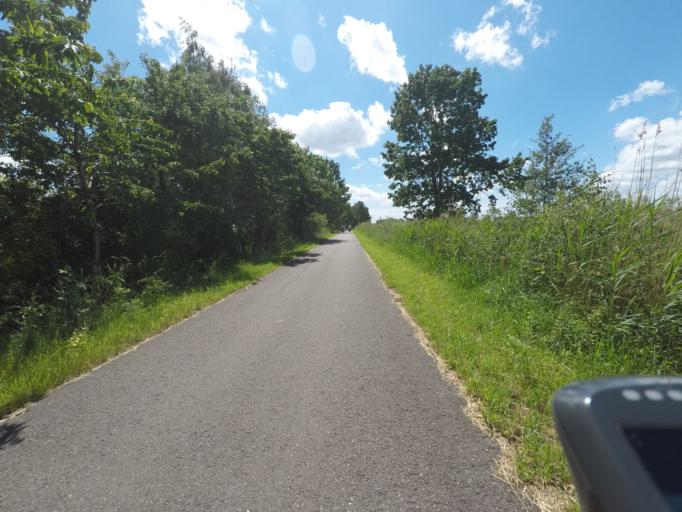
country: DE
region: Hamburg
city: Bergedorf
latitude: 53.4360
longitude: 10.2115
